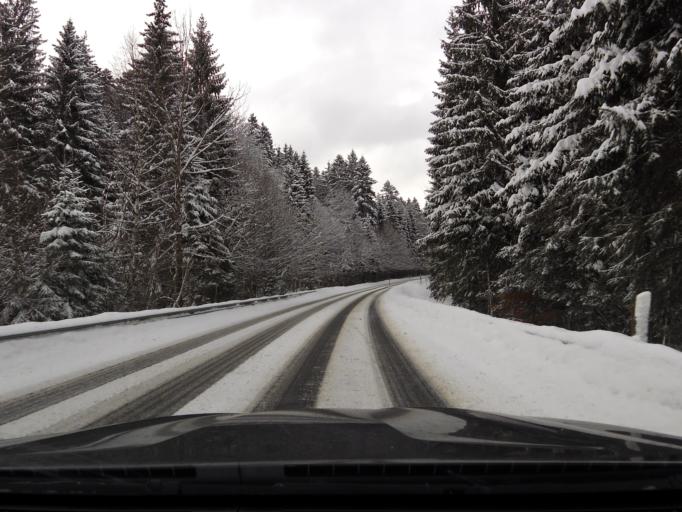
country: DE
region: Bavaria
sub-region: Lower Bavaria
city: Neuschonau
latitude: 48.9210
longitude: 13.4373
